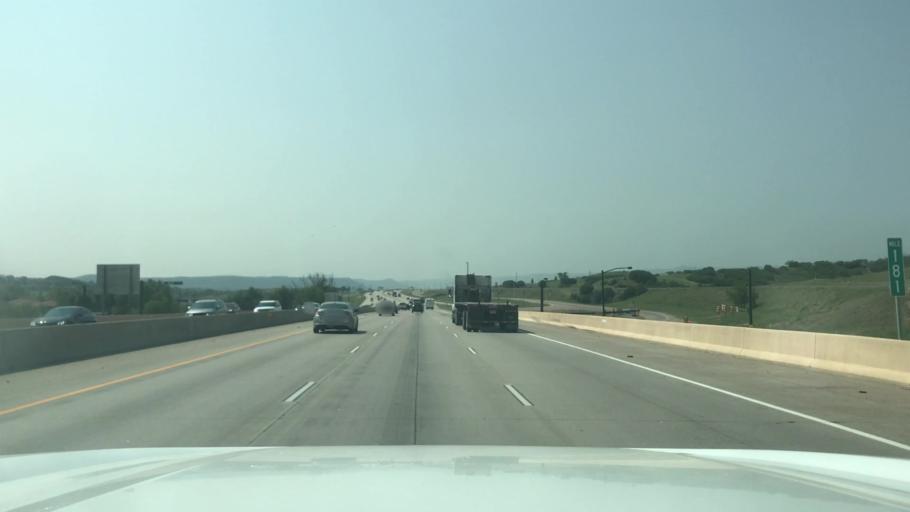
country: US
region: Colorado
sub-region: Douglas County
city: Castle Rock
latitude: 39.3677
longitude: -104.8653
